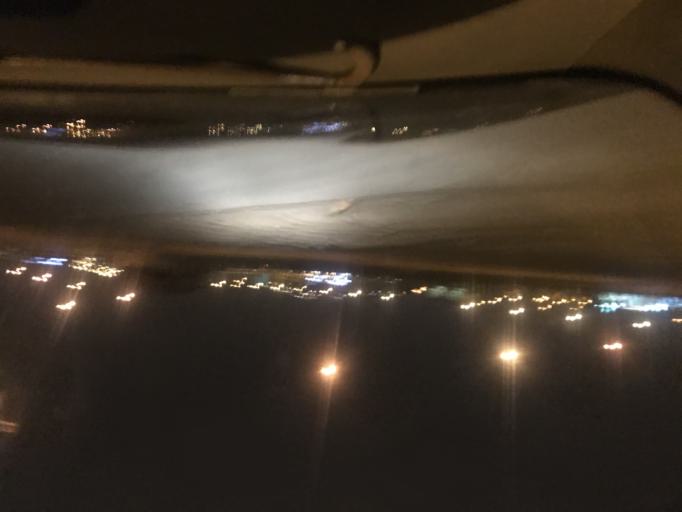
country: SA
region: Ar Riyad
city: Riyadh
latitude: 24.8066
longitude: 46.6746
